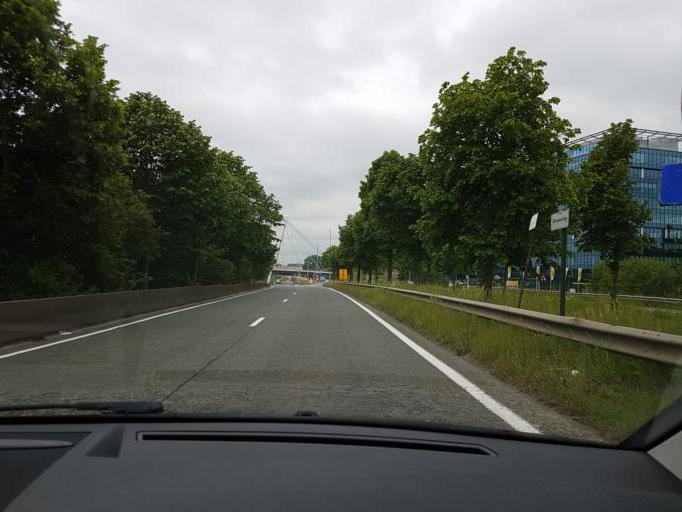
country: BE
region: Flanders
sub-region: Provincie Oost-Vlaanderen
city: Merelbeke
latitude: 51.0121
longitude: 3.7381
